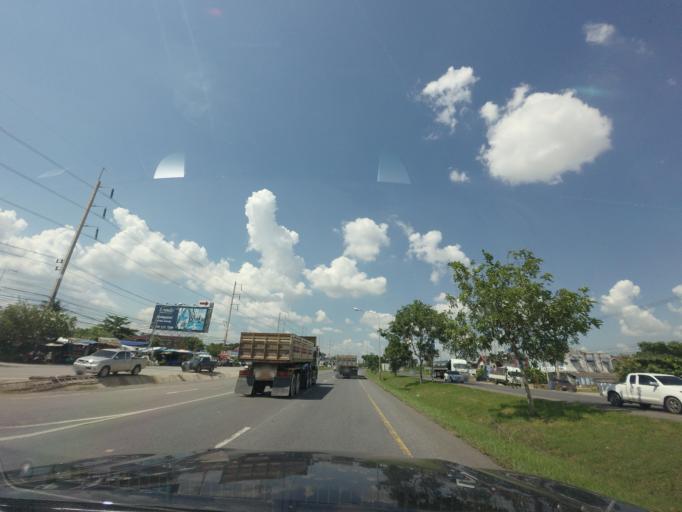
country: TH
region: Nakhon Ratchasima
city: Nakhon Ratchasima
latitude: 14.9734
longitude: 102.0519
